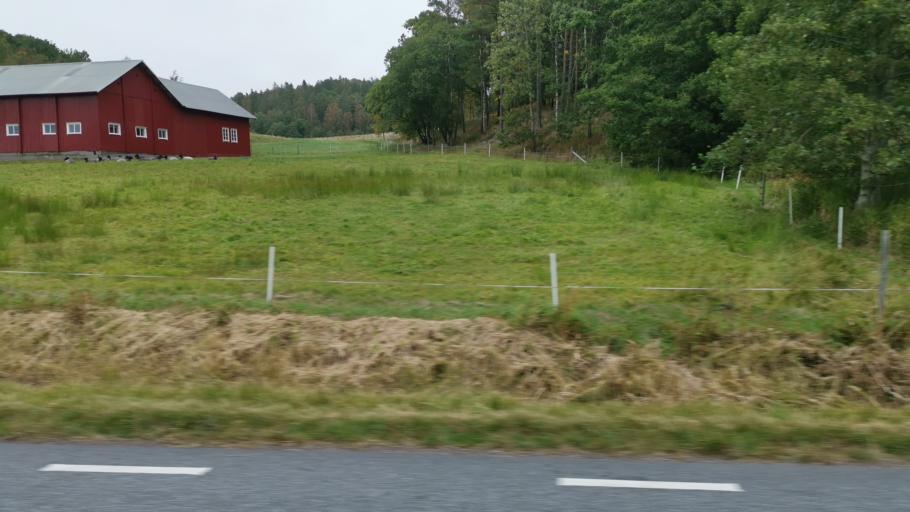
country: SE
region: Vaestra Goetaland
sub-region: Sotenas Kommun
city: Hunnebostrand
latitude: 58.5476
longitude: 11.4158
